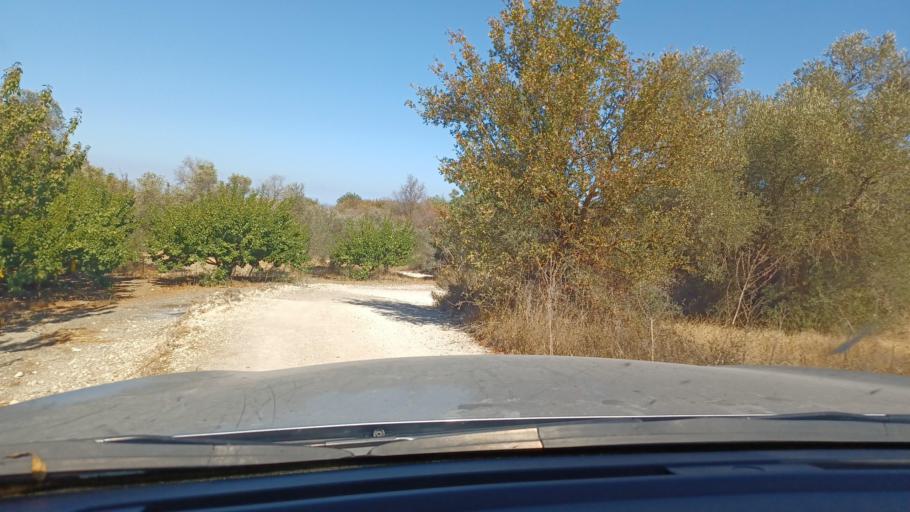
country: CY
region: Pafos
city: Polis
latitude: 35.0083
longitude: 32.5046
